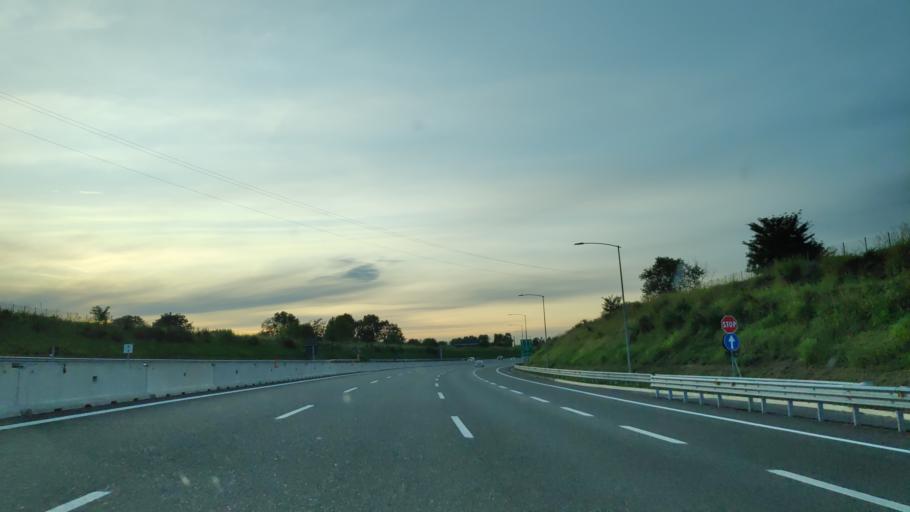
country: IT
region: Lombardy
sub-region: Citta metropolitana di Milano
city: Gorgonzola
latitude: 45.5487
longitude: 9.4126
